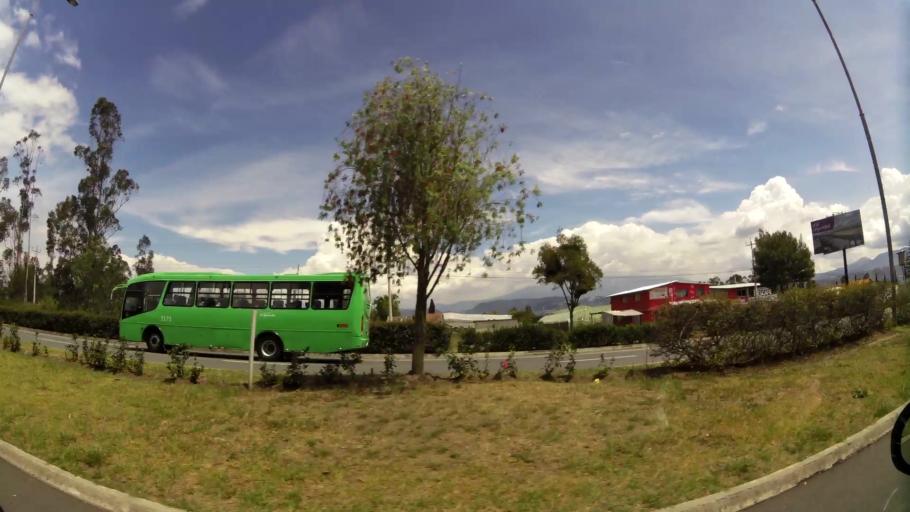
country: EC
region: Pichincha
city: Quito
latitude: -0.1573
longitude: -78.3484
